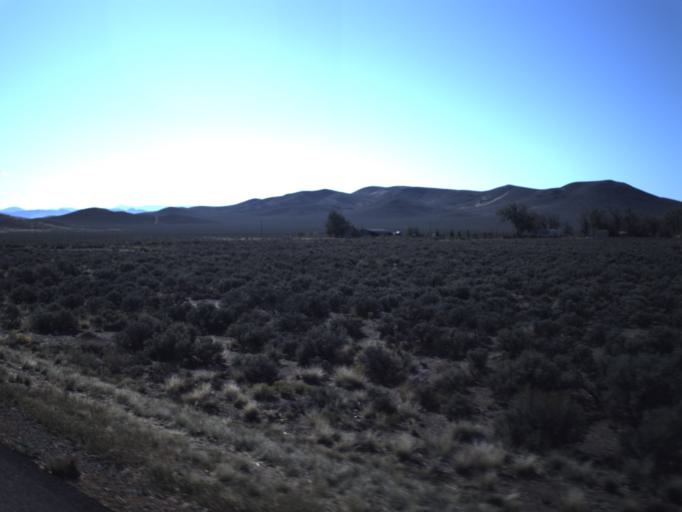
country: US
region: Utah
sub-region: Washington County
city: Enterprise
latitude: 37.7492
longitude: -113.7675
